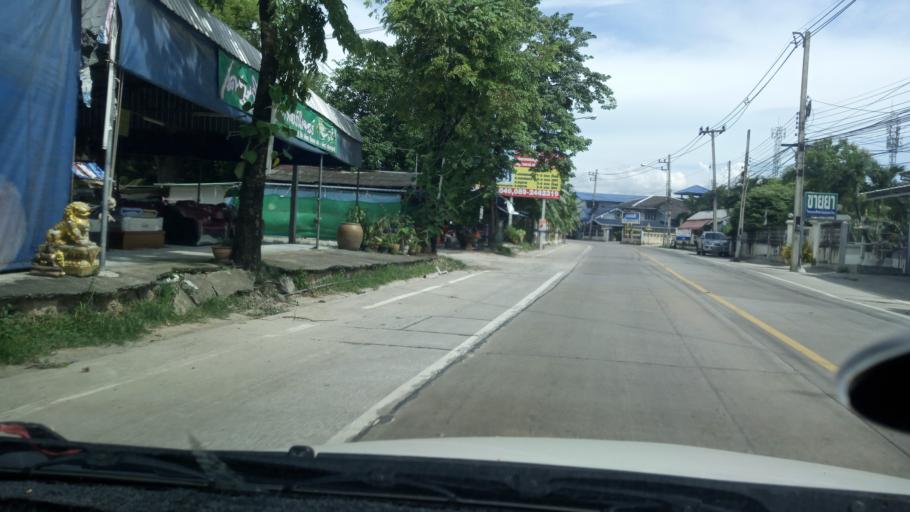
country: TH
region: Chon Buri
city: Chon Buri
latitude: 13.4102
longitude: 101.0283
